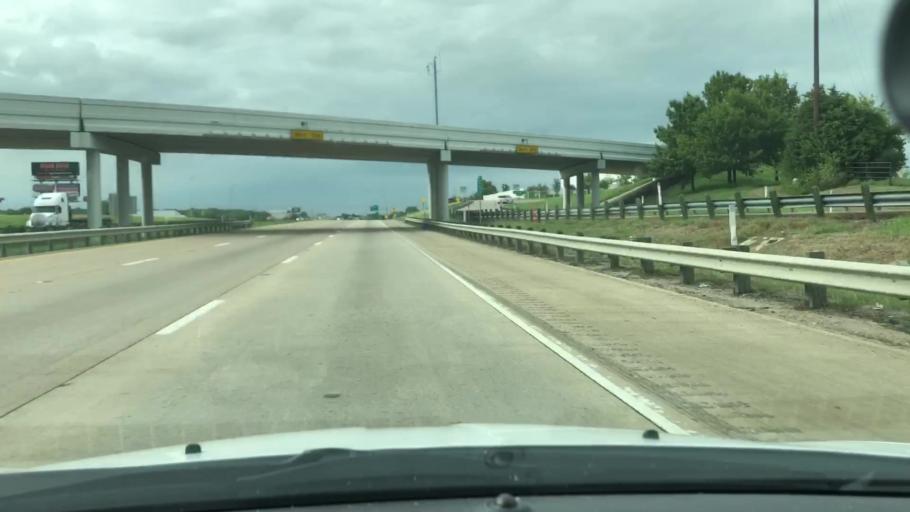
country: US
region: Texas
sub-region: Ellis County
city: Ennis
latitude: 32.3475
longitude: -96.6237
